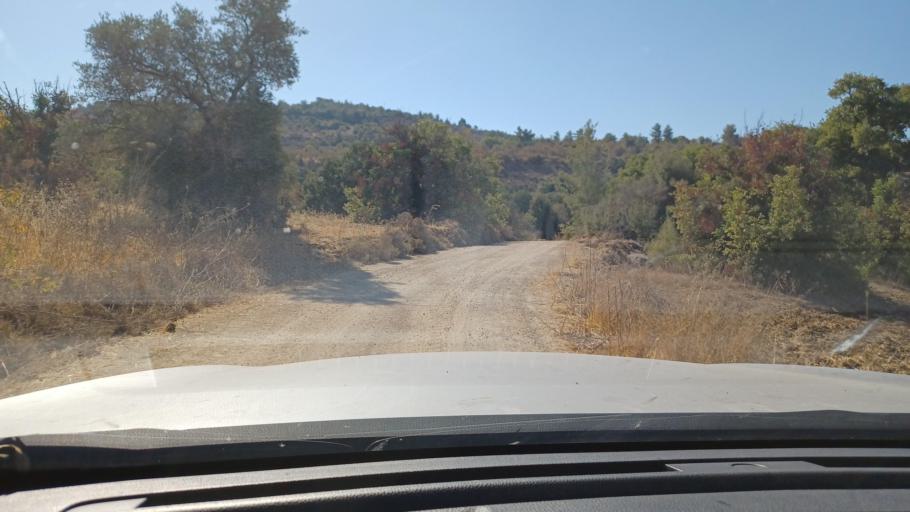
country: CY
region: Pafos
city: Polis
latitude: 35.0097
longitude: 32.5085
